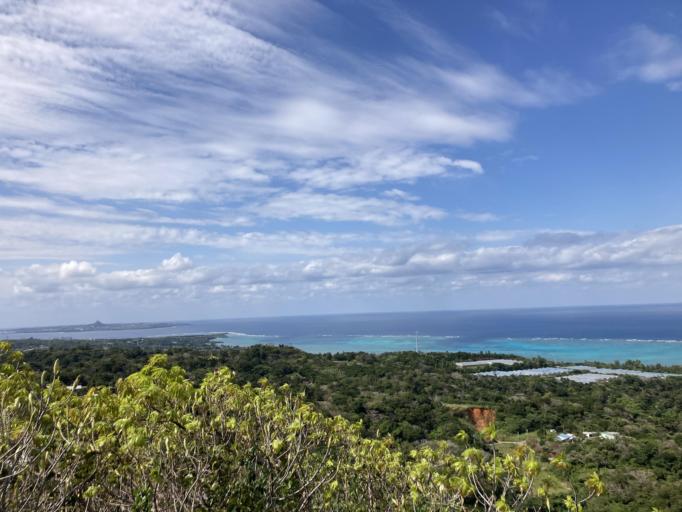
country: JP
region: Okinawa
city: Nago
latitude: 26.6878
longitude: 127.9266
